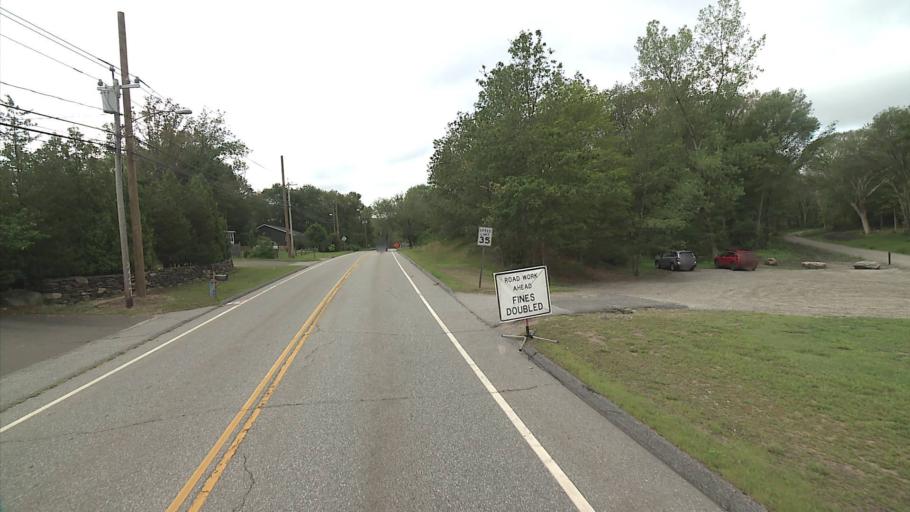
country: US
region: Connecticut
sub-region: New London County
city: Colchester
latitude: 41.5844
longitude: -72.4001
